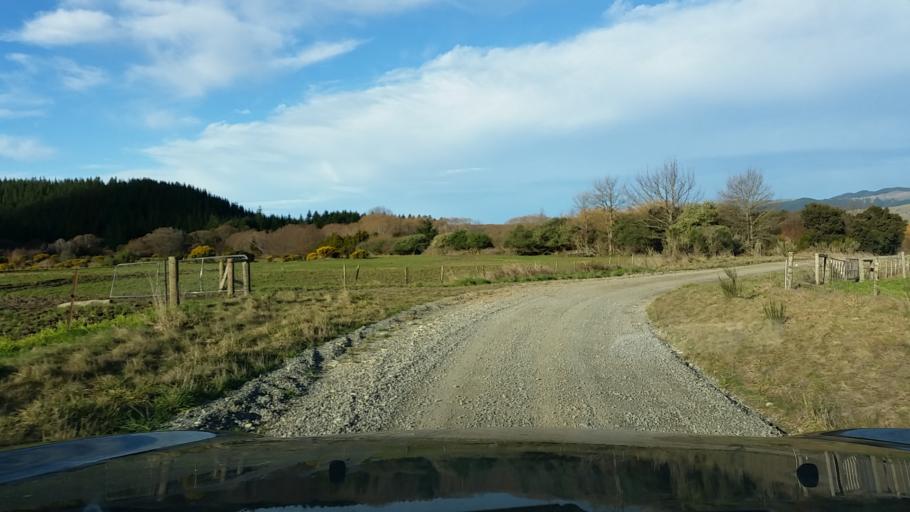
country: NZ
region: Nelson
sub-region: Nelson City
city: Nelson
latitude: -41.5649
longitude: 173.4477
